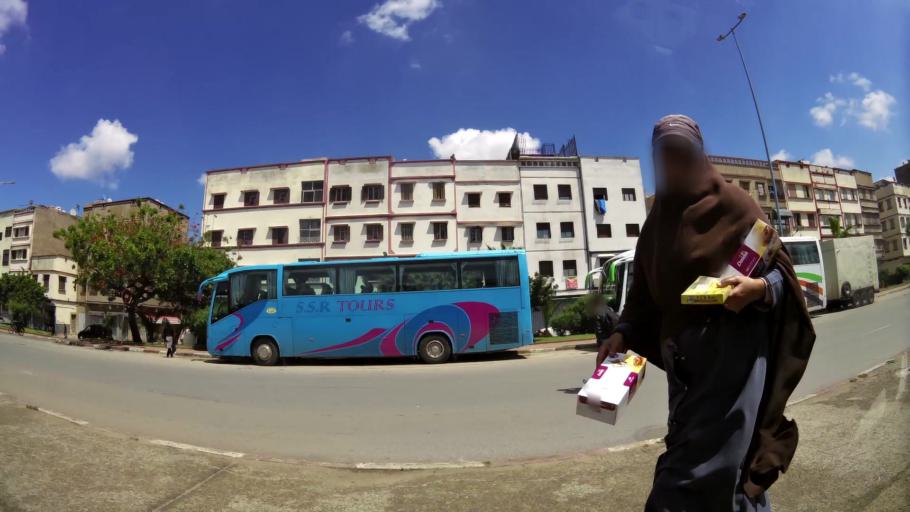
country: MA
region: Grand Casablanca
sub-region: Casablanca
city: Casablanca
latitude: 33.5448
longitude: -7.5827
